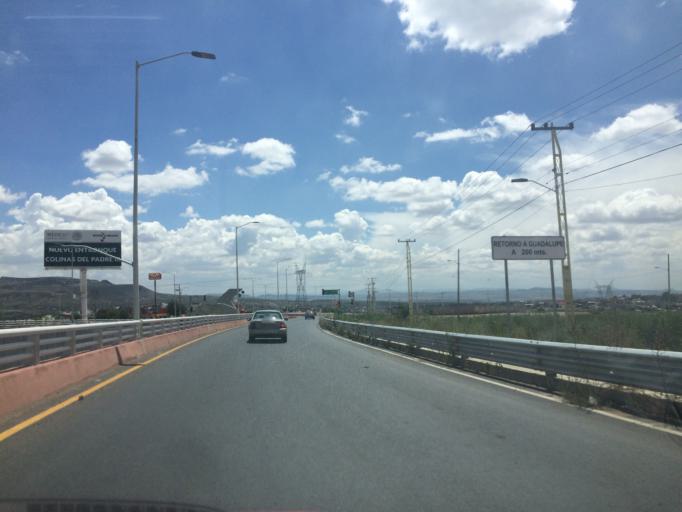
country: MX
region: Zacatecas
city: Zacatecas
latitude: 22.7503
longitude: -102.5896
